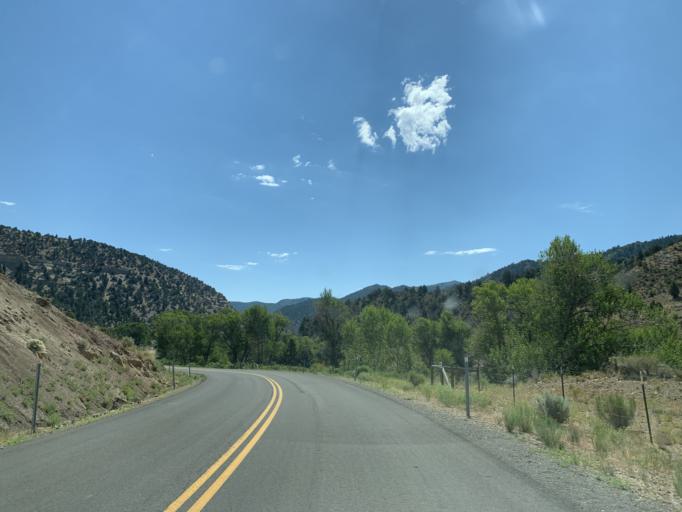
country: US
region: Utah
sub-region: Carbon County
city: East Carbon City
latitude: 39.7762
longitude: -110.4754
